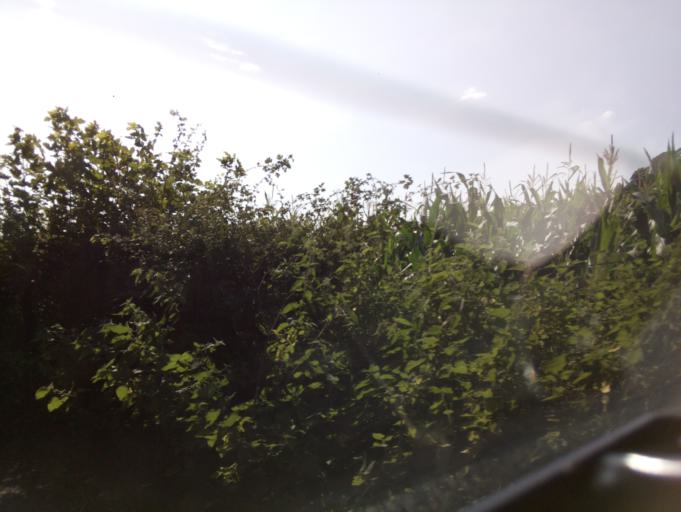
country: GB
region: England
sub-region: Gloucestershire
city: Dursley
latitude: 51.6906
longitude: -2.3189
